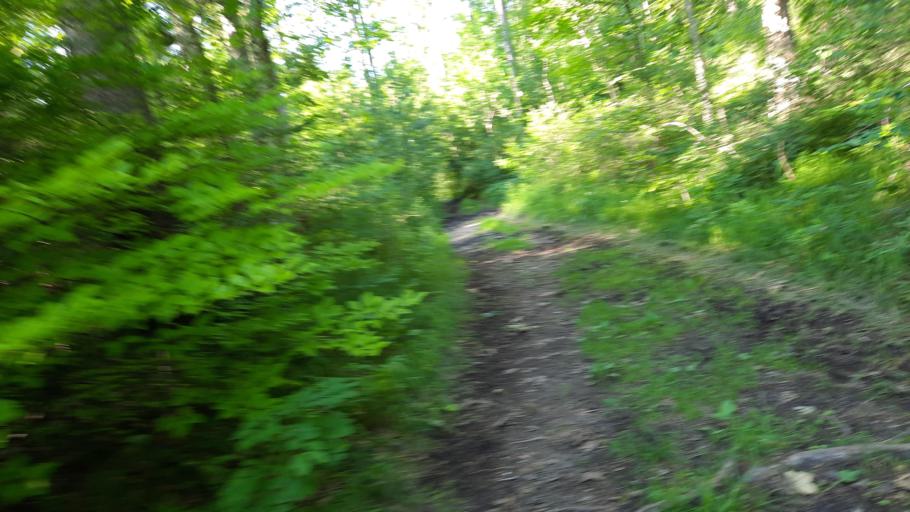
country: DE
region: Bavaria
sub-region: Upper Bavaria
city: Glonn
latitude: 47.9607
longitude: 11.9038
